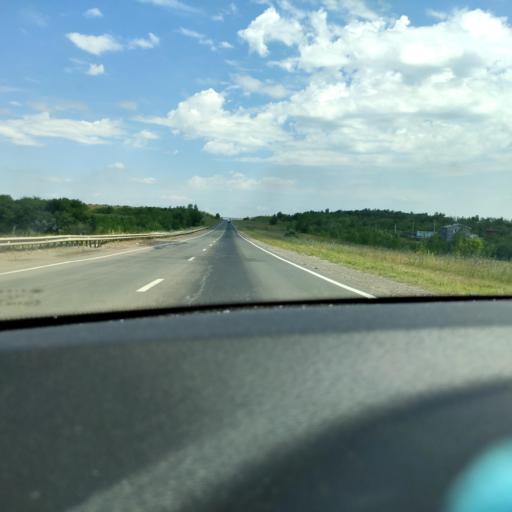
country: RU
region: Samara
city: Petra-Dubrava
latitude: 53.2935
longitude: 50.3916
